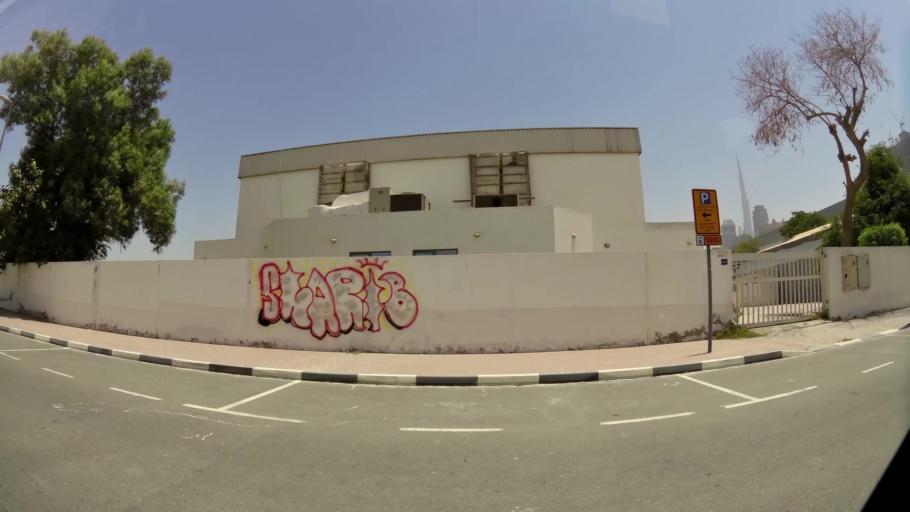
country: AE
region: Dubai
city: Dubai
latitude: 25.1890
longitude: 55.2524
